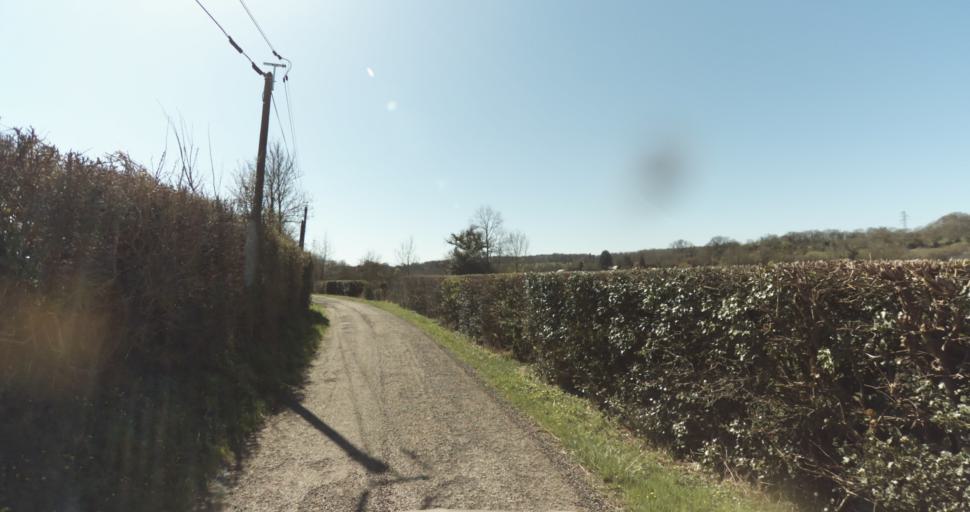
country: FR
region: Lower Normandy
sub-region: Departement du Calvados
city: Livarot
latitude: 48.9981
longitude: 0.0969
